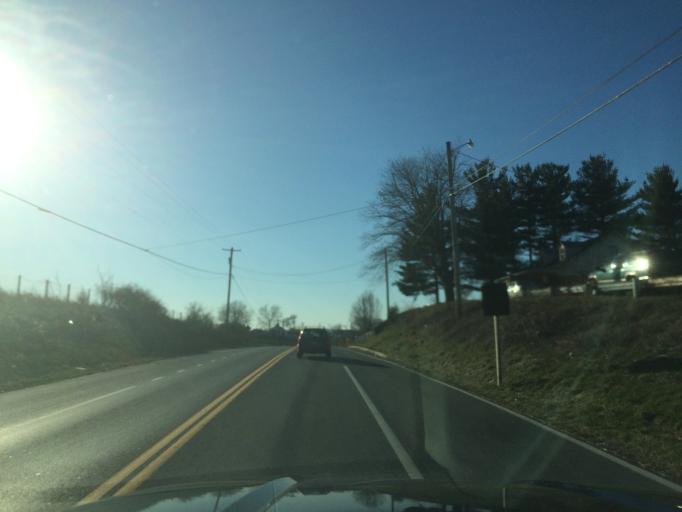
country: US
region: Maryland
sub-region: Frederick County
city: Spring Ridge
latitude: 39.3893
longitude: -77.3081
